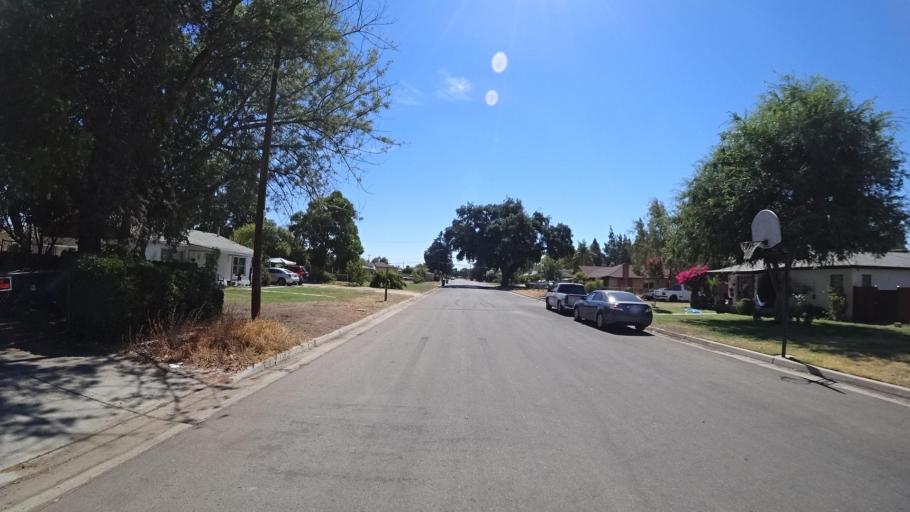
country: US
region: California
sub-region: Fresno County
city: Sunnyside
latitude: 36.7459
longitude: -119.7289
